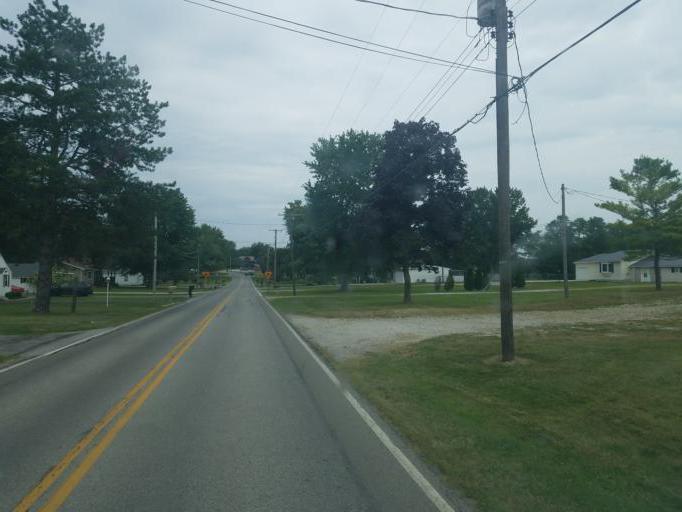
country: US
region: Ohio
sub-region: Marion County
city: Marion
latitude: 40.5474
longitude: -83.1368
